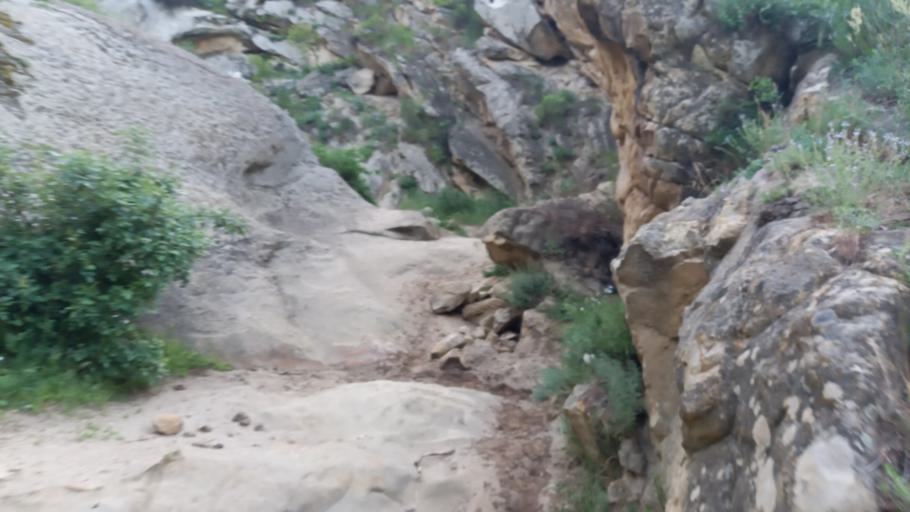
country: RU
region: Dagestan
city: Korkmaskala
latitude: 42.9793
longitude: 47.2446
